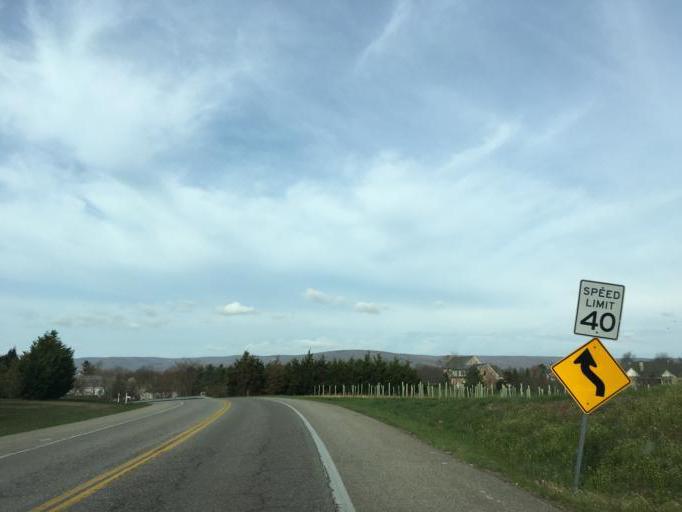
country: US
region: Maryland
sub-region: Frederick County
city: Walkersville
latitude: 39.5089
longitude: -77.3985
